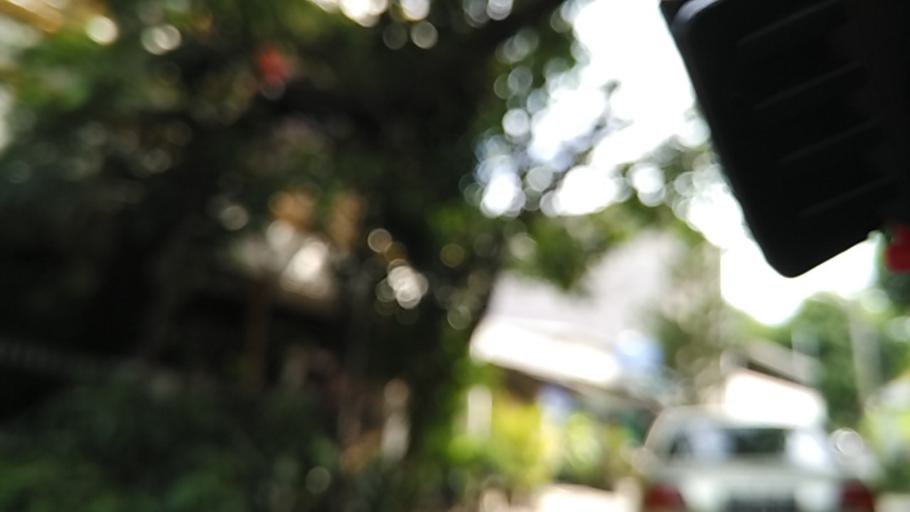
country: ID
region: Central Java
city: Semarang
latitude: -7.0002
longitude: 110.4241
